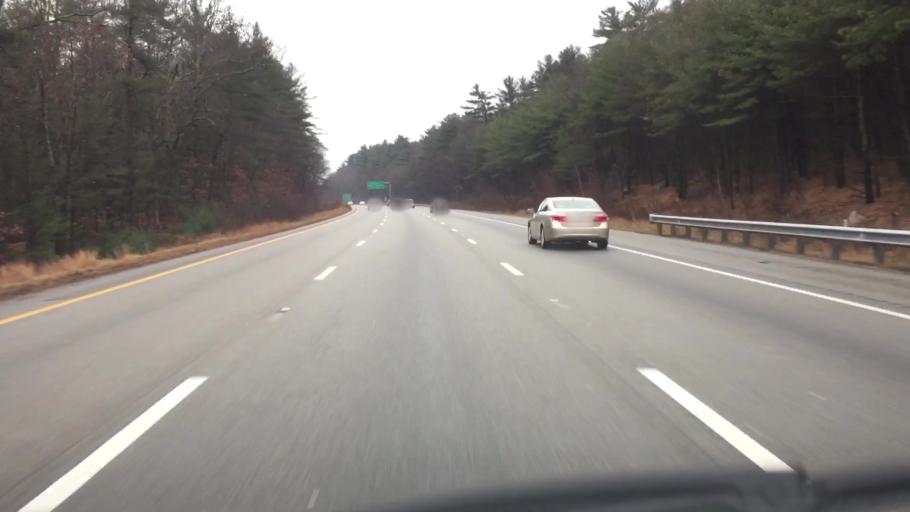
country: US
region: Massachusetts
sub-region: Worcester County
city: Cordaville
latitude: 42.2515
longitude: -71.5574
